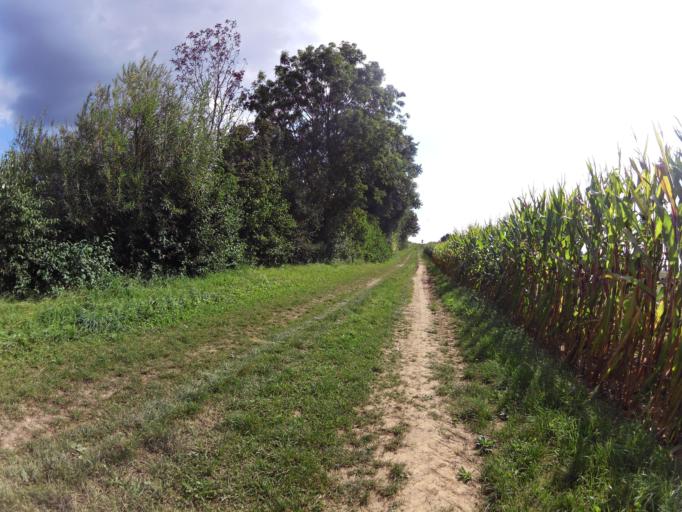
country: DE
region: Bavaria
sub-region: Regierungsbezirk Unterfranken
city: Oberpleichfeld
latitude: 49.8602
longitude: 10.1048
